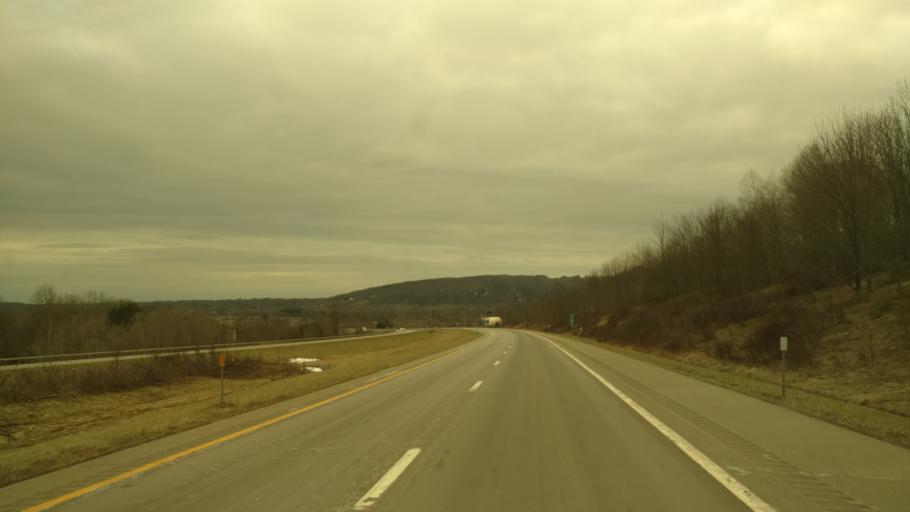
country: US
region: New York
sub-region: Chautauqua County
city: Falconer
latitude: 42.1381
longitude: -79.1727
